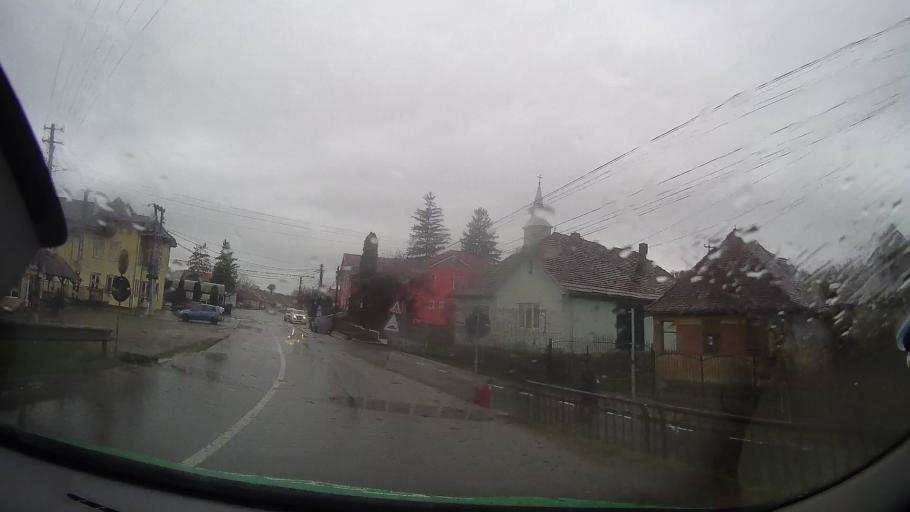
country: RO
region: Bistrita-Nasaud
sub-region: Comuna Monor
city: Monor
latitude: 46.9502
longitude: 24.6934
